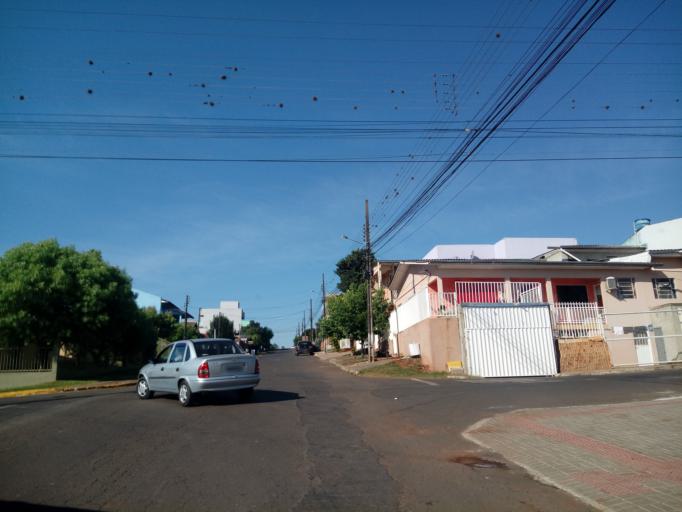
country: BR
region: Santa Catarina
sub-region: Chapeco
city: Chapeco
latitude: -27.0980
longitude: -52.6696
